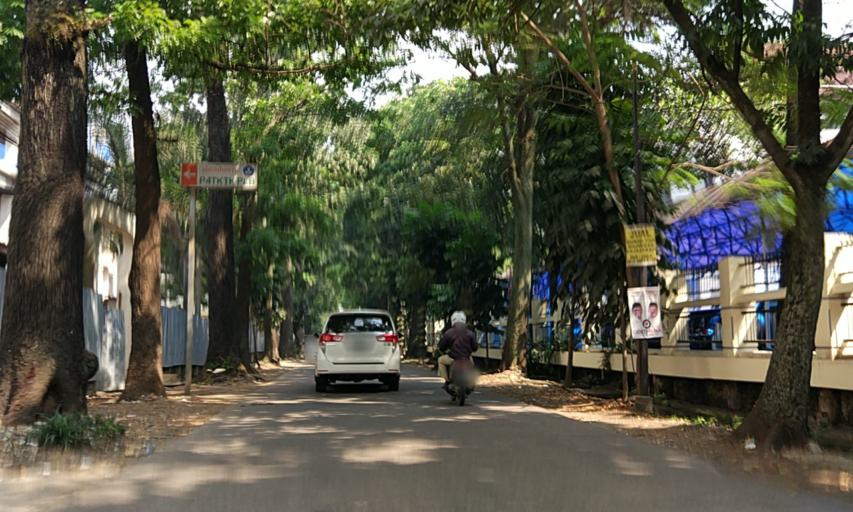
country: ID
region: West Java
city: Bandung
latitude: -6.9049
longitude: 107.6004
